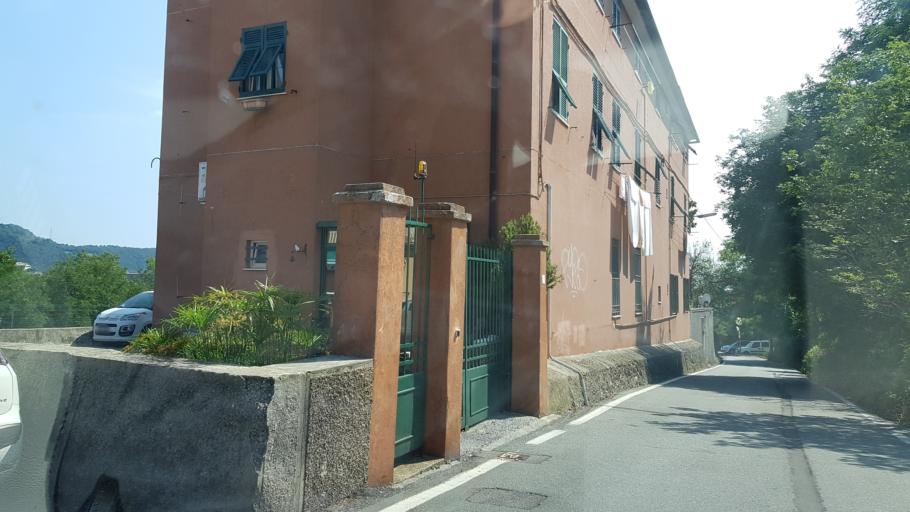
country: IT
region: Liguria
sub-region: Provincia di Genova
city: Genoa
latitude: 44.4477
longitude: 8.9014
